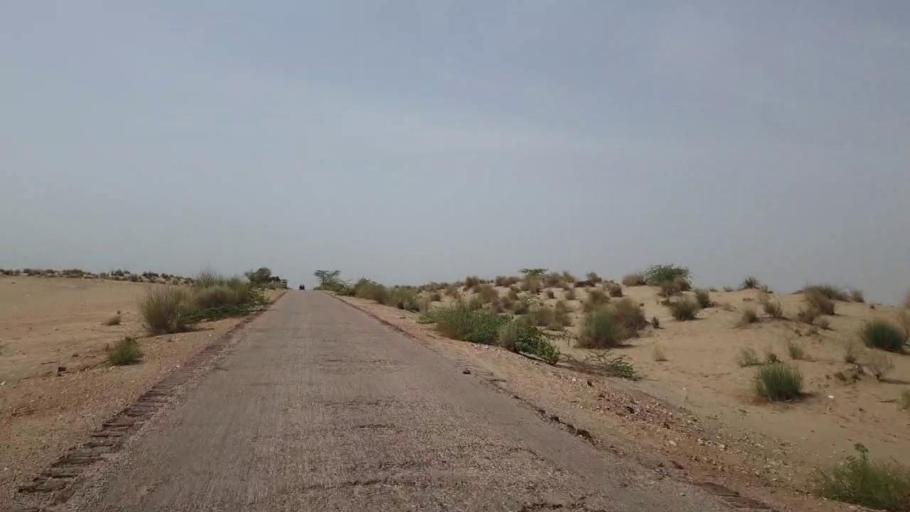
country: PK
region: Sindh
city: Bandhi
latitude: 26.5563
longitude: 68.3829
